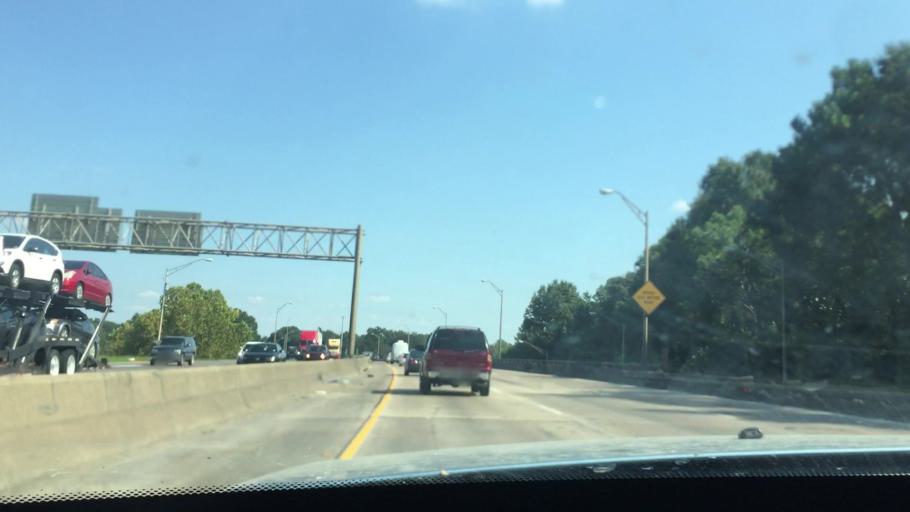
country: US
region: Louisiana
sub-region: East Baton Rouge Parish
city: Baton Rouge
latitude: 30.4278
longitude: -91.1703
